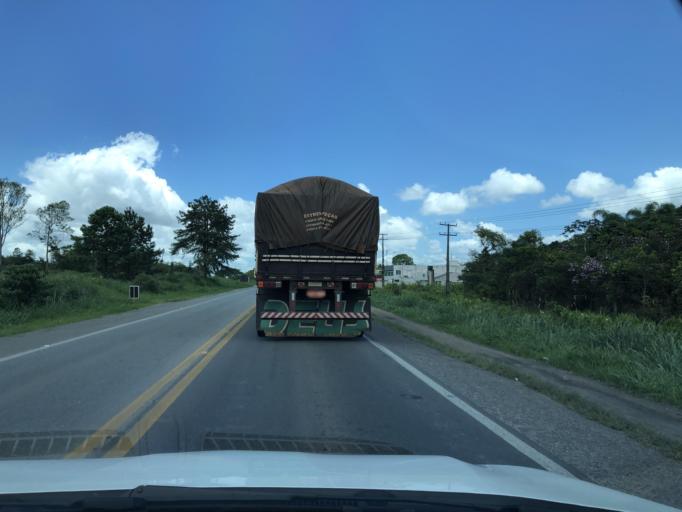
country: BR
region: Santa Catarina
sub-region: Sao Francisco Do Sul
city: Sao Francisco do Sul
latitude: -26.3710
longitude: -48.7030
